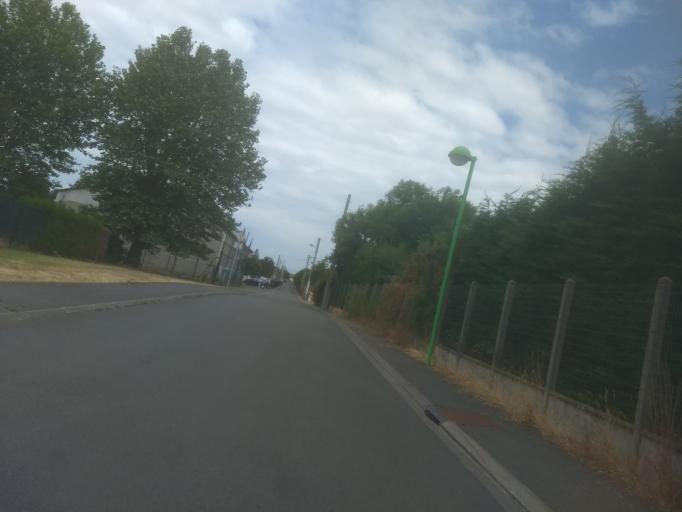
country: FR
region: Nord-Pas-de-Calais
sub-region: Departement du Pas-de-Calais
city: Beaurains
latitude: 50.2737
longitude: 2.7810
